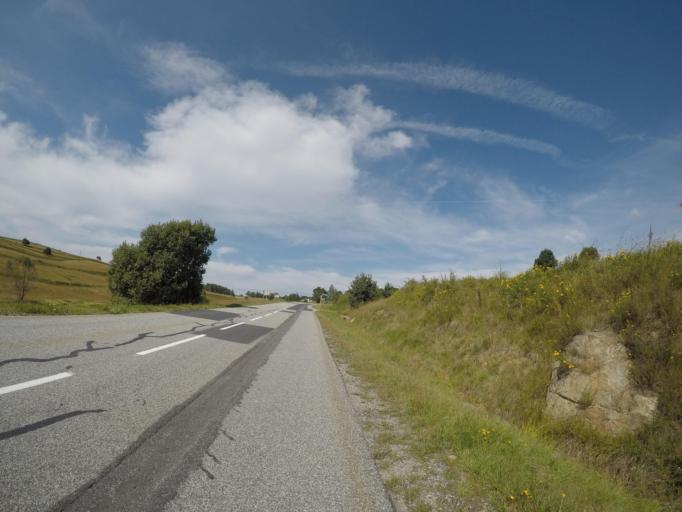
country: ES
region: Catalonia
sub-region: Provincia de Girona
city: Llivia
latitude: 42.4996
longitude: 2.1021
